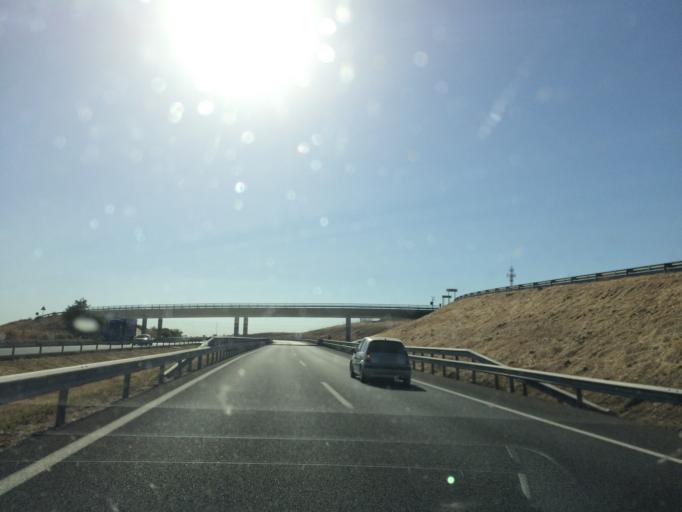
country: ES
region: Castille-La Mancha
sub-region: Province of Toledo
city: Quismondo
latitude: 40.1144
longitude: -4.3156
